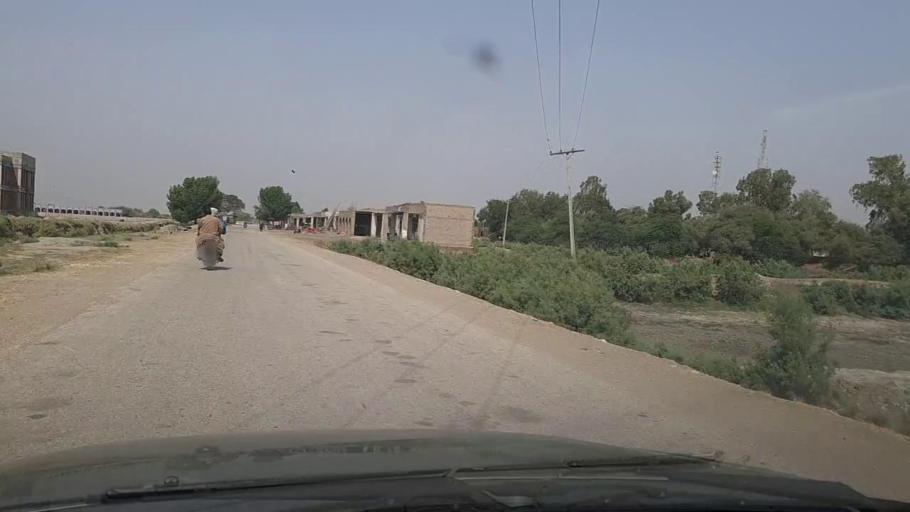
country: PK
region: Sindh
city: Thul
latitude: 28.3234
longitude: 68.7400
